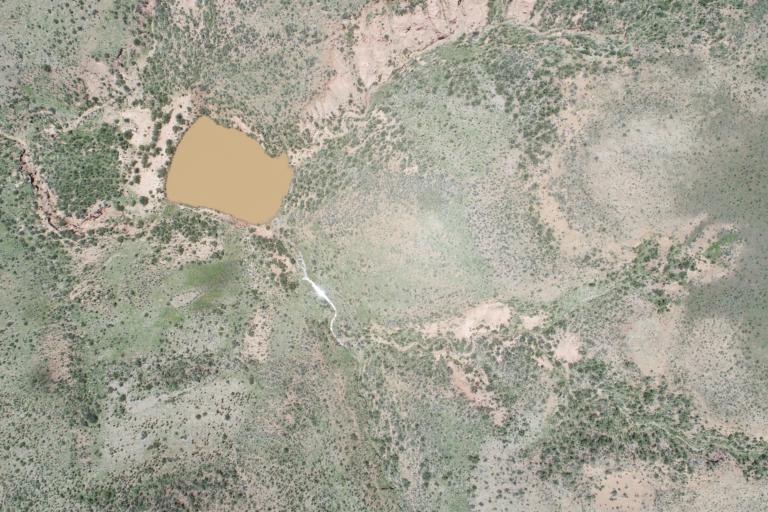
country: BO
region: La Paz
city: Curahuara de Carangas
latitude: -17.3098
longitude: -68.5015
